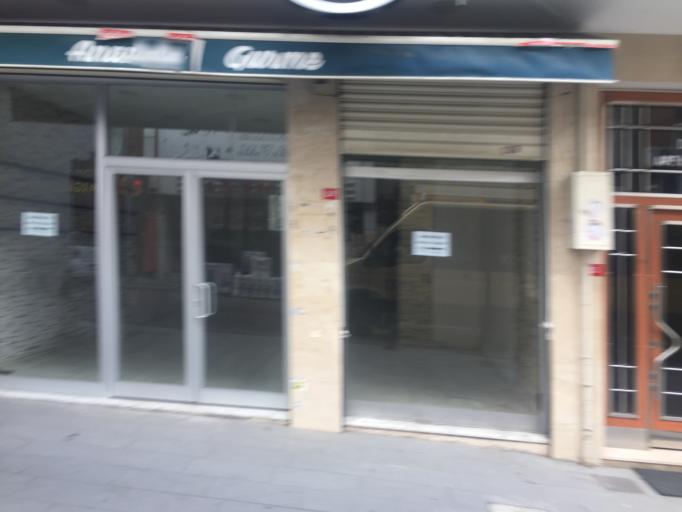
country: TR
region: Istanbul
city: Esenler
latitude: 41.0463
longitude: 28.9057
